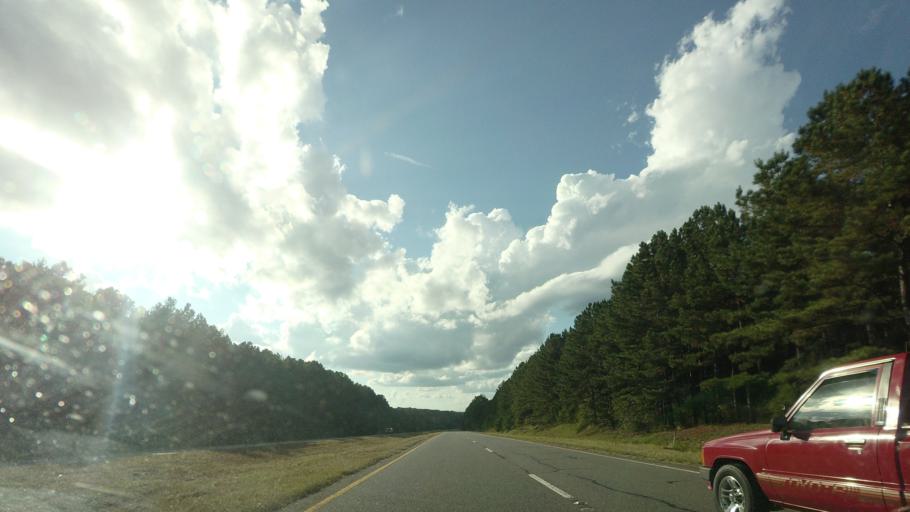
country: US
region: Georgia
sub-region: Houston County
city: Perry
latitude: 32.3928
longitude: -83.6286
